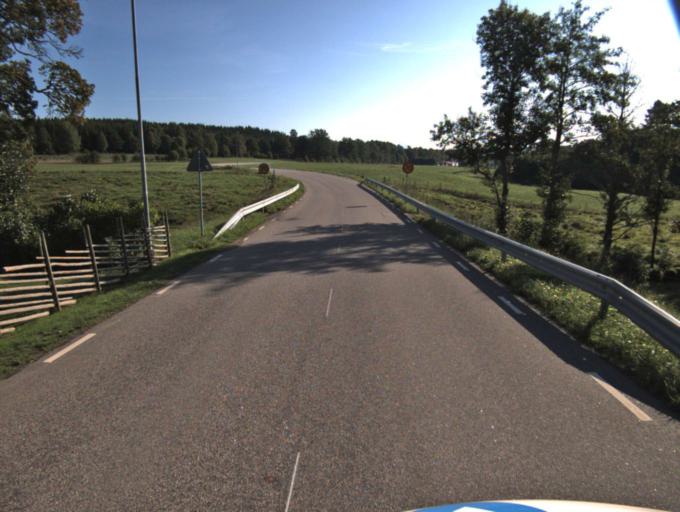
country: SE
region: Vaestra Goetaland
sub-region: Ulricehamns Kommun
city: Ulricehamn
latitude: 57.7983
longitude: 13.3788
